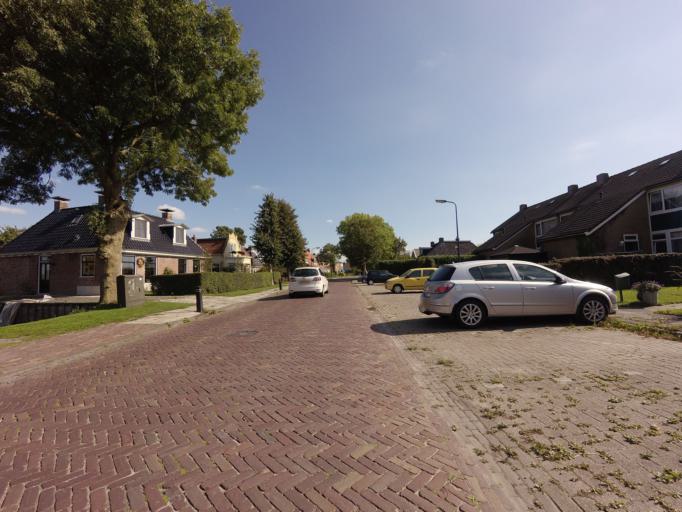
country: NL
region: Friesland
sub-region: Gemeente Littenseradiel
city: Makkum
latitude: 53.1004
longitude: 5.6452
